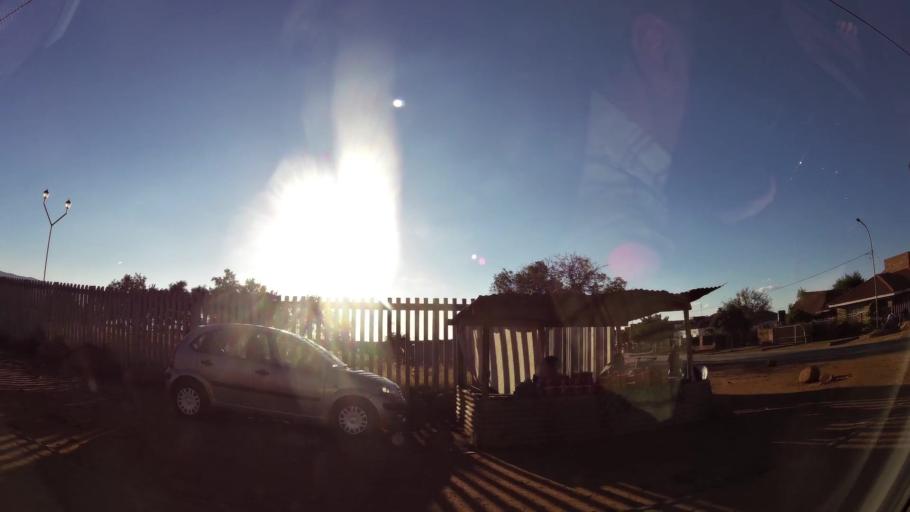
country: ZA
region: Limpopo
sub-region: Waterberg District Municipality
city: Mokopane
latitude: -24.1441
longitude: 28.9905
